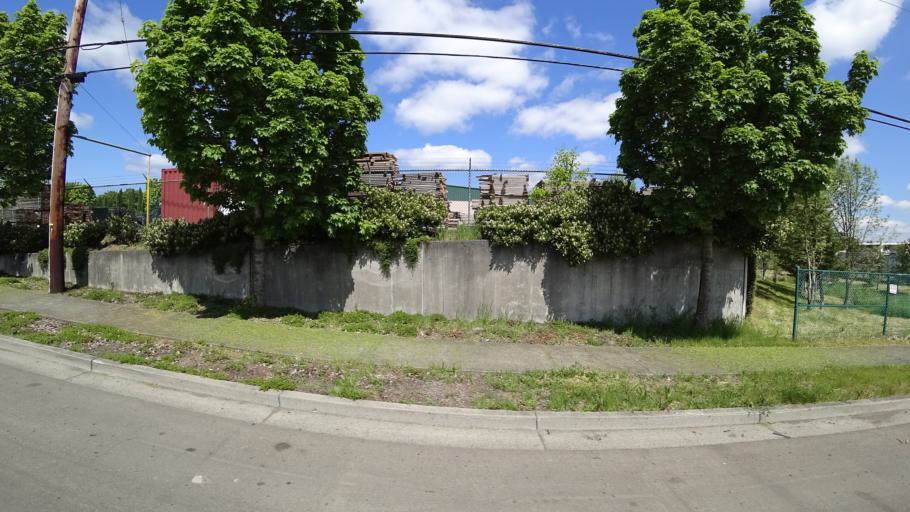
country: US
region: Oregon
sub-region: Washington County
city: Hillsboro
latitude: 45.5128
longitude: -122.9938
